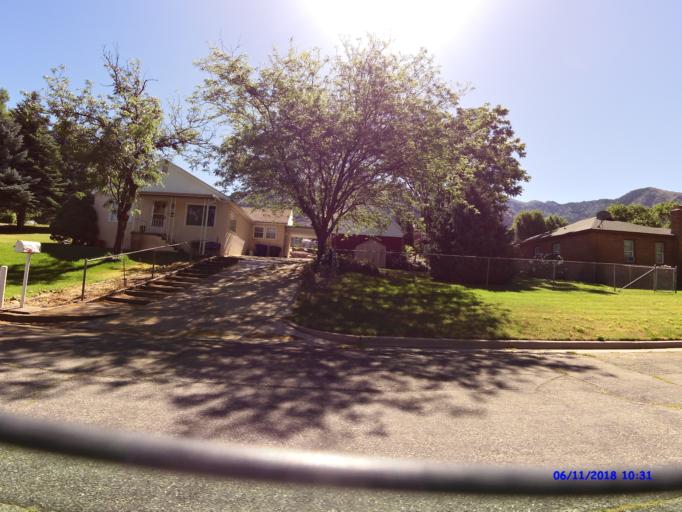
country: US
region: Utah
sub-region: Weber County
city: Ogden
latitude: 41.2270
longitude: -111.9411
